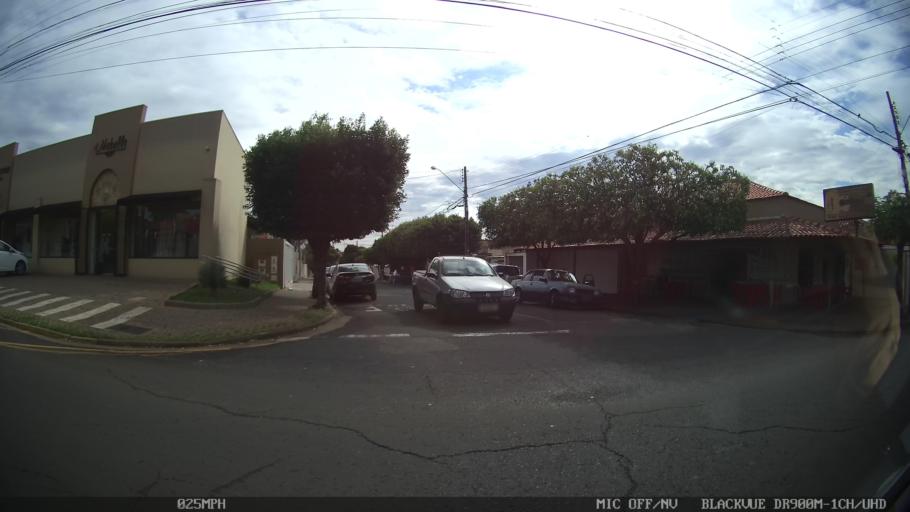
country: BR
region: Sao Paulo
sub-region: Sao Jose Do Rio Preto
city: Sao Jose do Rio Preto
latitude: -20.8167
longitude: -49.3677
